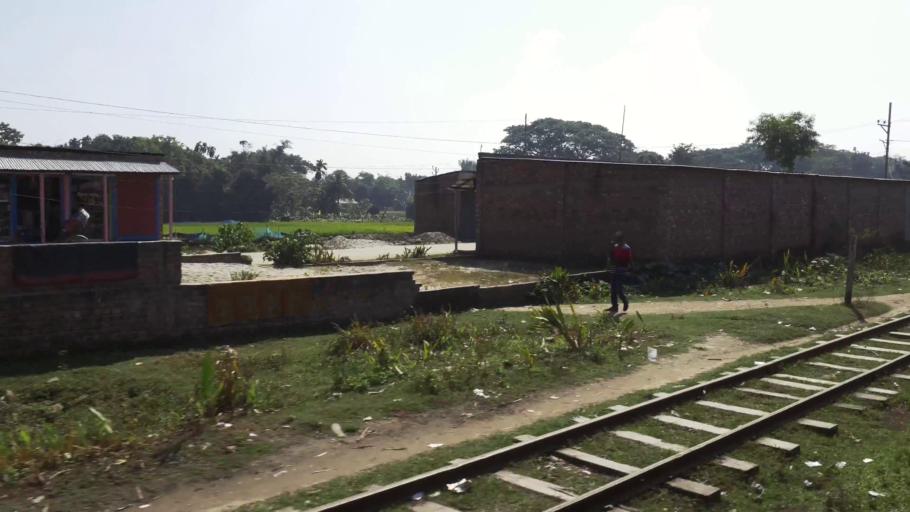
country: BD
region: Dhaka
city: Gafargaon
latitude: 24.4944
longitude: 90.5241
